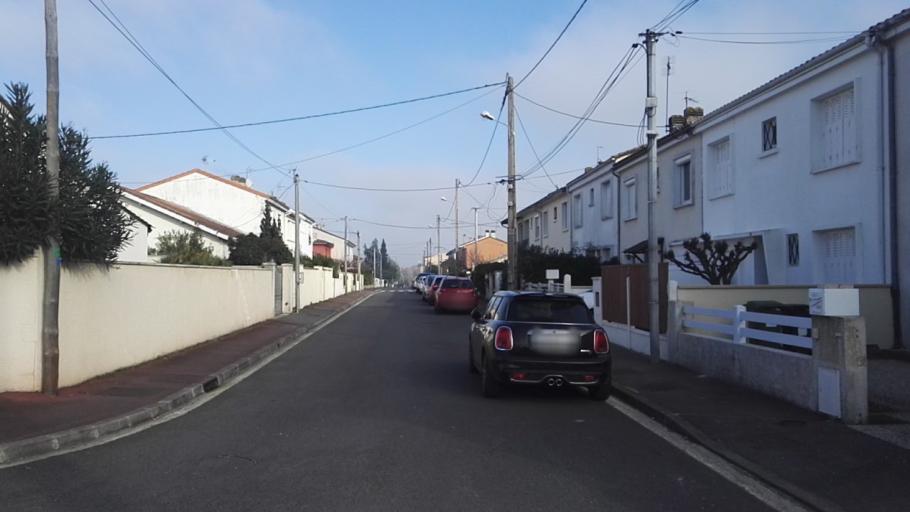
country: FR
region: Aquitaine
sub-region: Departement de la Gironde
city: Talence
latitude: 44.8030
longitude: -0.5840
